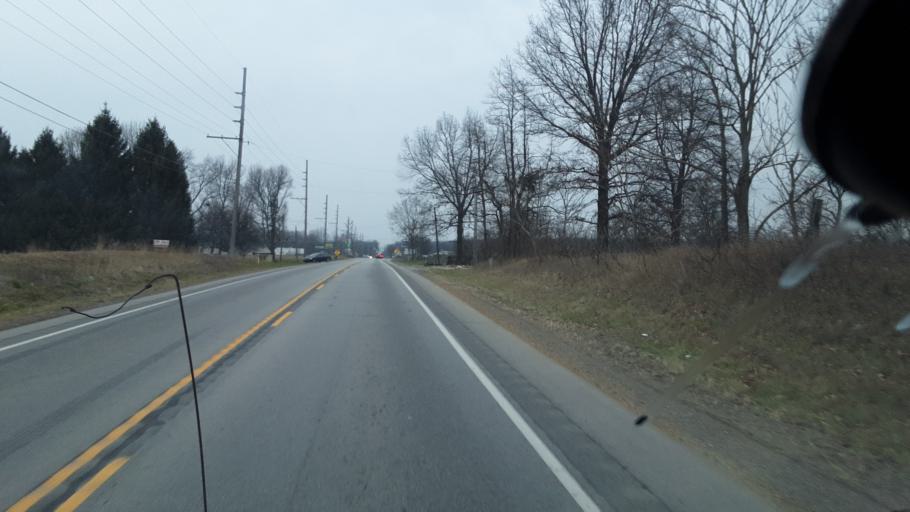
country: US
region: Indiana
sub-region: Elkhart County
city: Middlebury
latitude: 41.7213
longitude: -85.6846
